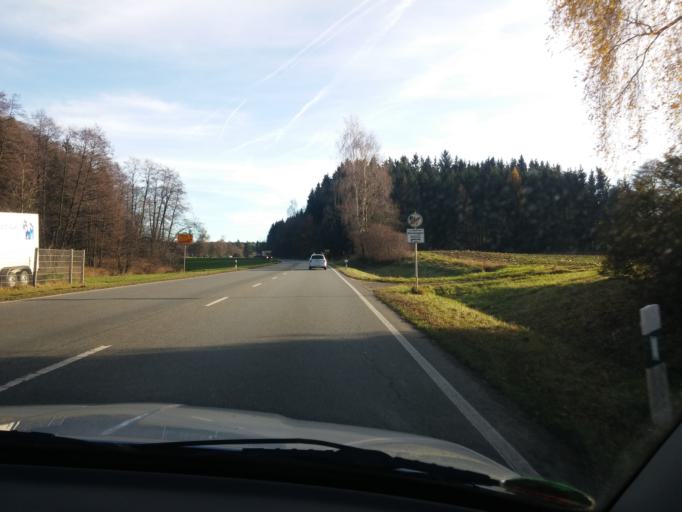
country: DE
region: Bavaria
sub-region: Upper Bavaria
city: Schnaitsee
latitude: 48.0390
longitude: 12.3378
